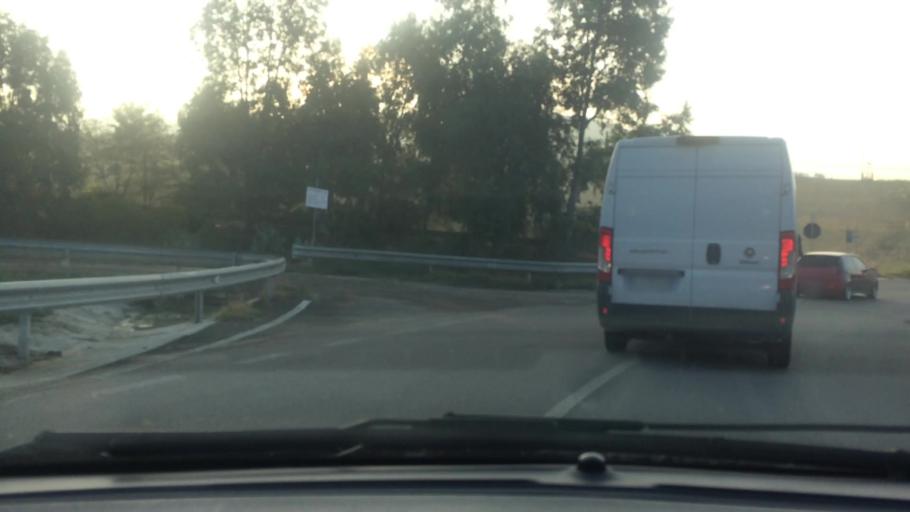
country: IT
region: Basilicate
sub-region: Provincia di Matera
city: Montescaglioso
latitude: 40.5353
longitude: 16.6454
